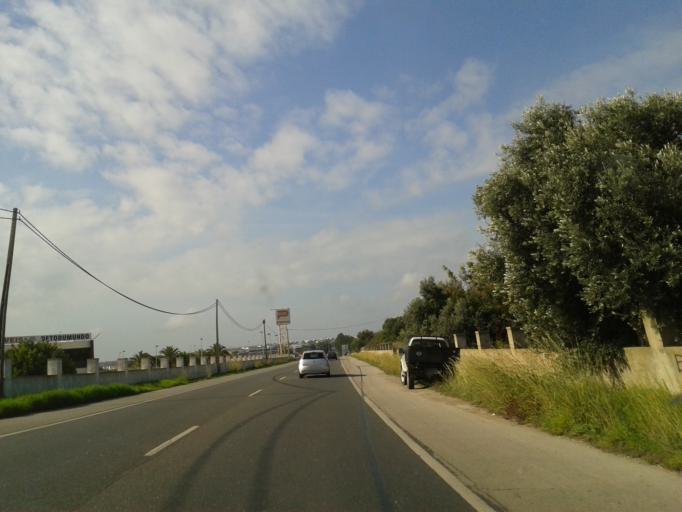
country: PT
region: Faro
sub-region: Tavira
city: Tavira
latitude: 37.1348
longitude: -7.6289
